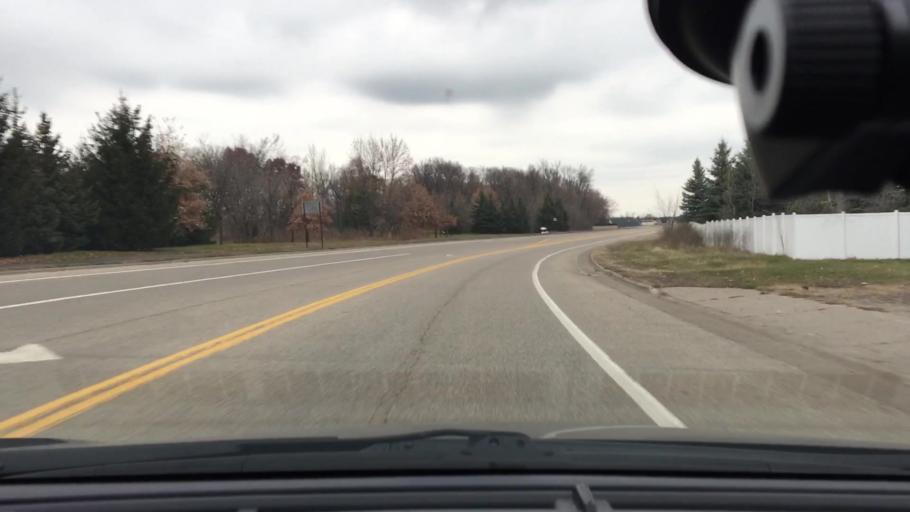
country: US
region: Minnesota
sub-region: Hennepin County
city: Corcoran
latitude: 45.0503
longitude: -93.5244
